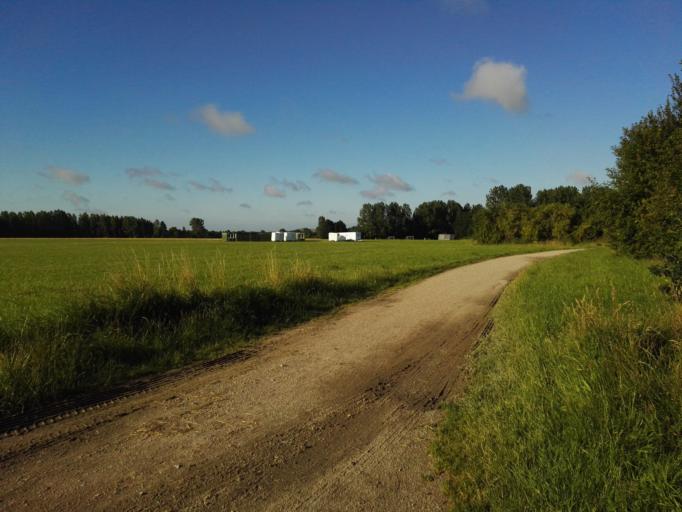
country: DK
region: Capital Region
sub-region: Ballerup Kommune
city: Ballerup
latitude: 55.7187
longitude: 12.3812
